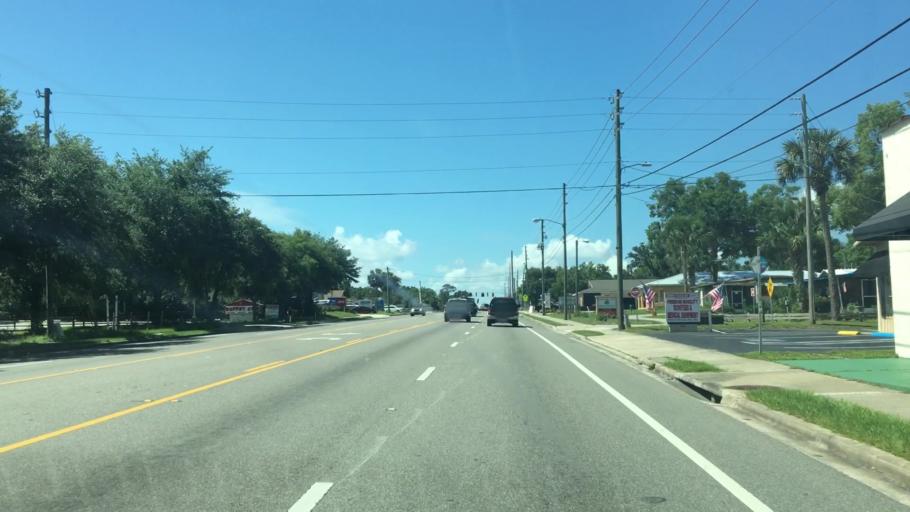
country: US
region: Florida
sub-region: Volusia County
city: Orange City
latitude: 28.9368
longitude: -81.2990
